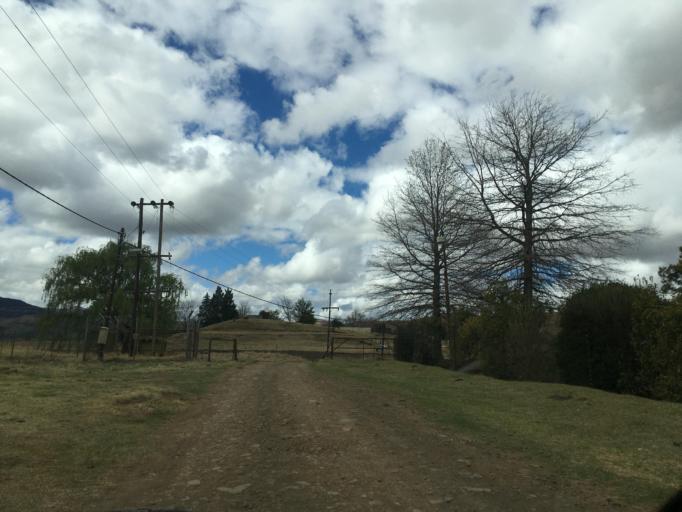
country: ZA
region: Eastern Cape
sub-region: Chris Hani District Municipality
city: Elliot
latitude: -31.3285
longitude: 27.8567
